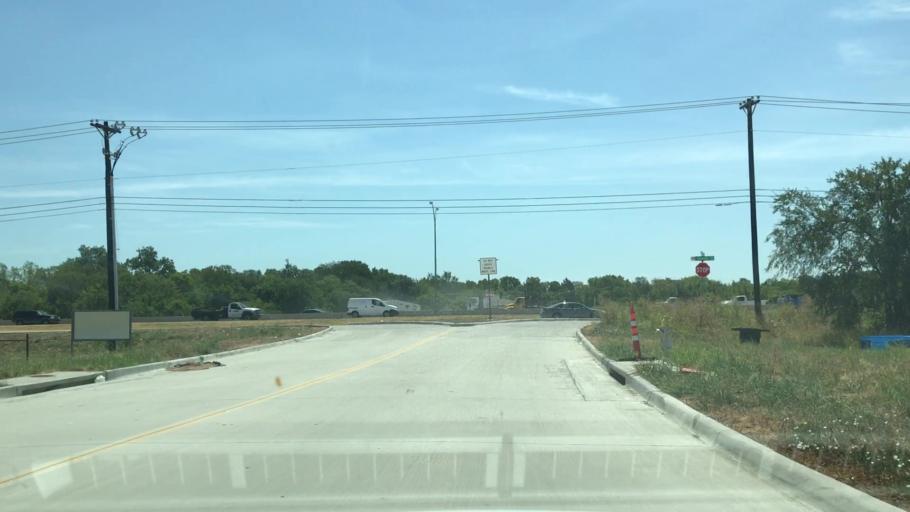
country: US
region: Texas
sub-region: Collin County
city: Allen
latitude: 33.1213
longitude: -96.6685
